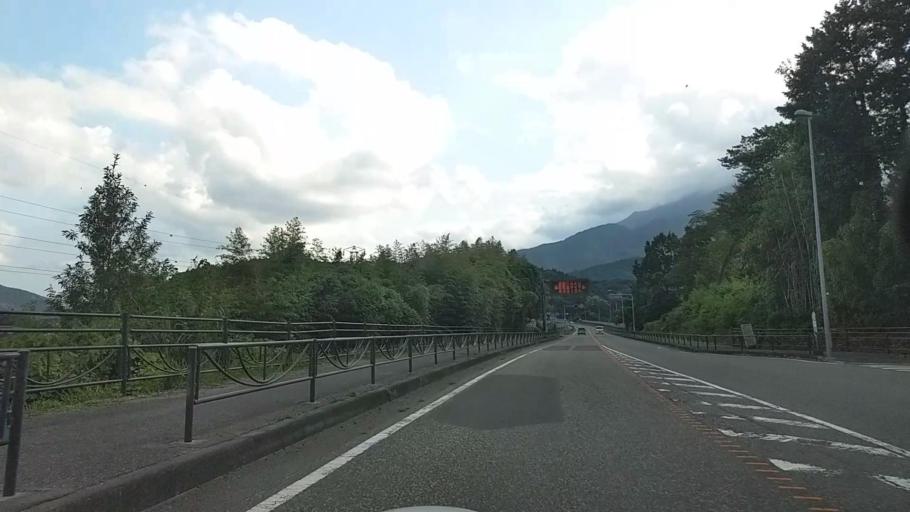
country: JP
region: Shizuoka
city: Fujinomiya
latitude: 35.2998
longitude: 138.4475
